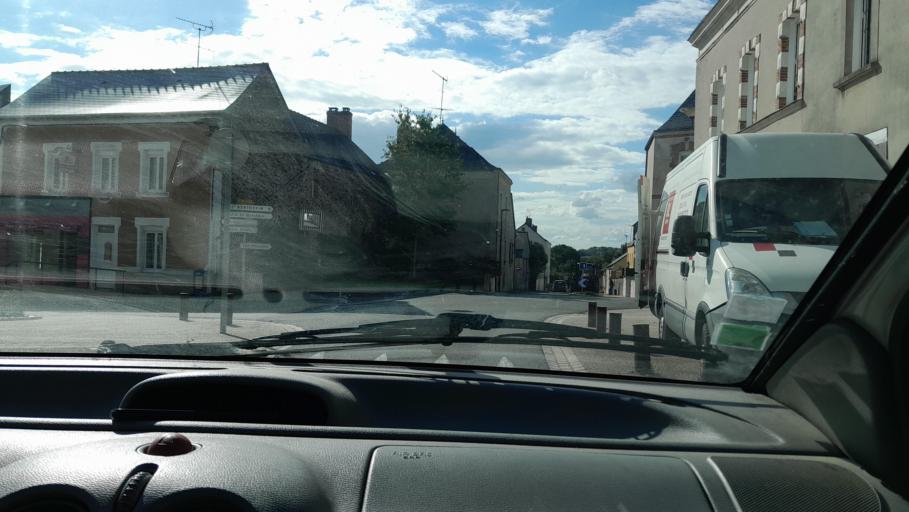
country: FR
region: Pays de la Loire
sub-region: Departement de la Mayenne
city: Ahuille
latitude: 48.0197
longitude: -0.8704
